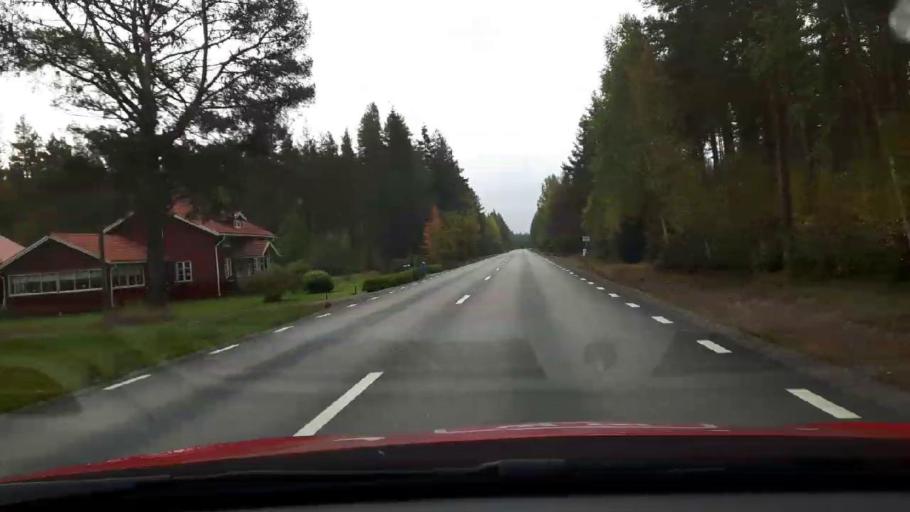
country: SE
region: Gaevleborg
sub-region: Ljusdals Kommun
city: Farila
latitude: 61.8573
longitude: 15.7451
